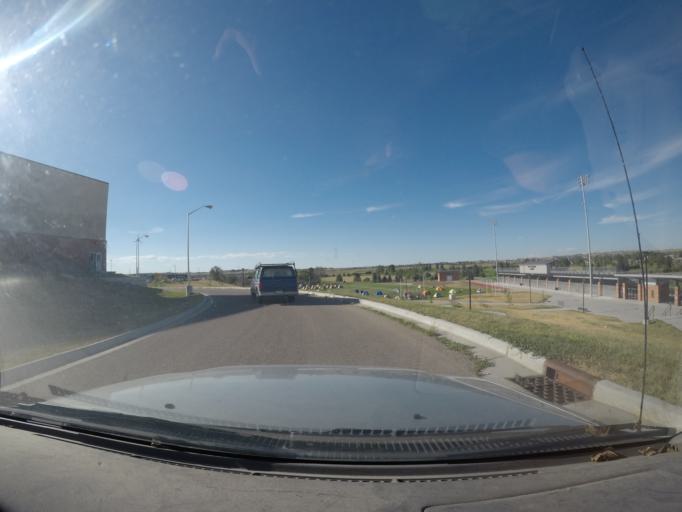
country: US
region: Wyoming
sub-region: Laramie County
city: Fox Farm-College
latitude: 41.1473
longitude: -104.7764
